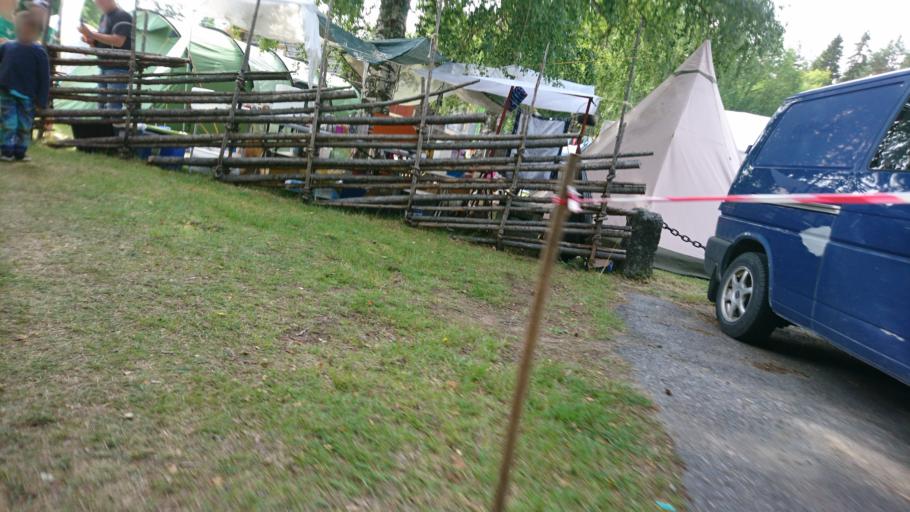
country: SE
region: Vaesternorrland
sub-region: Solleftea Kommun
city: As
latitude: 63.4454
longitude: 16.8837
